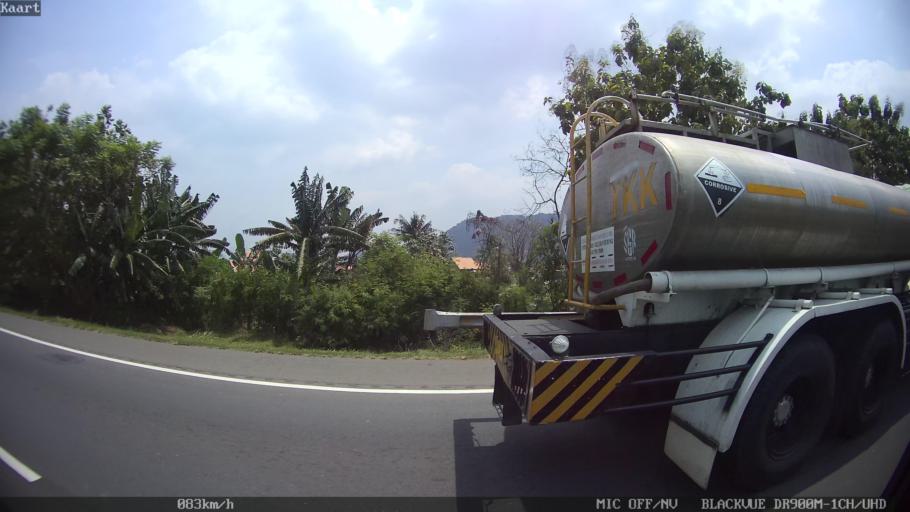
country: ID
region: Banten
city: Serang
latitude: -6.0535
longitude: 106.1187
